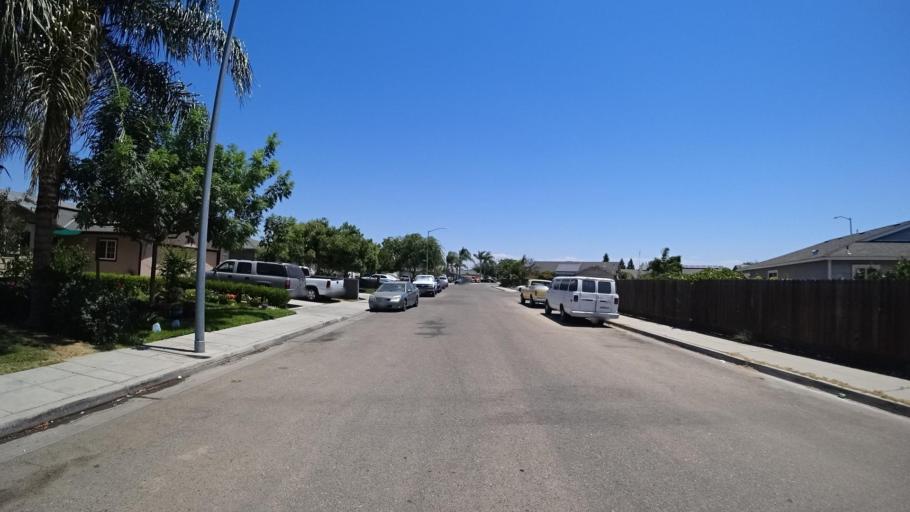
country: US
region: California
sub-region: Fresno County
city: Sunnyside
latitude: 36.7084
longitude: -119.7306
